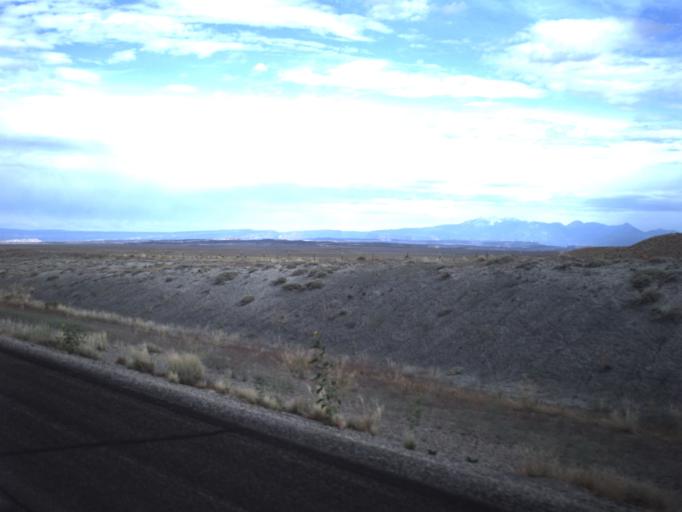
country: US
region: Utah
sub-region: Grand County
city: Moab
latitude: 38.9421
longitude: -109.6299
